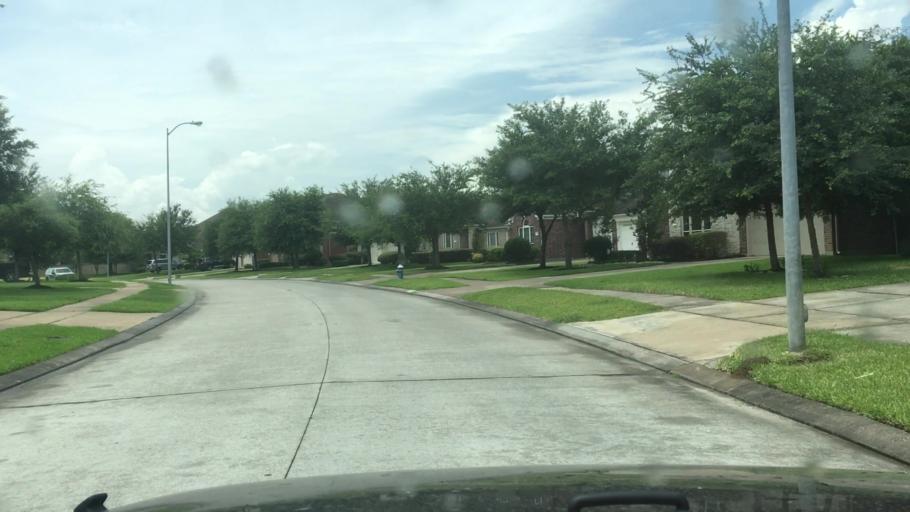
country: US
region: Texas
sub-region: Harris County
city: Humble
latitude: 29.9313
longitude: -95.2487
